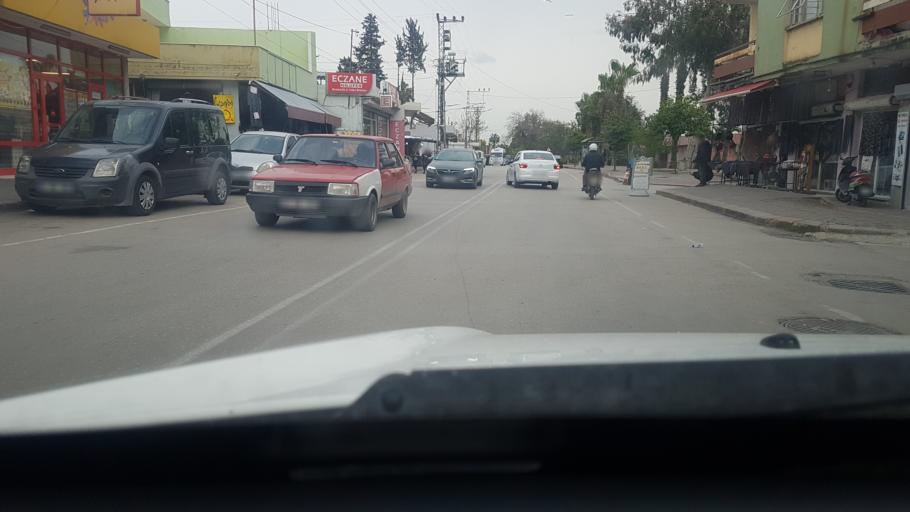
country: TR
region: Adana
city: Seyhan
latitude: 37.0135
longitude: 35.2792
